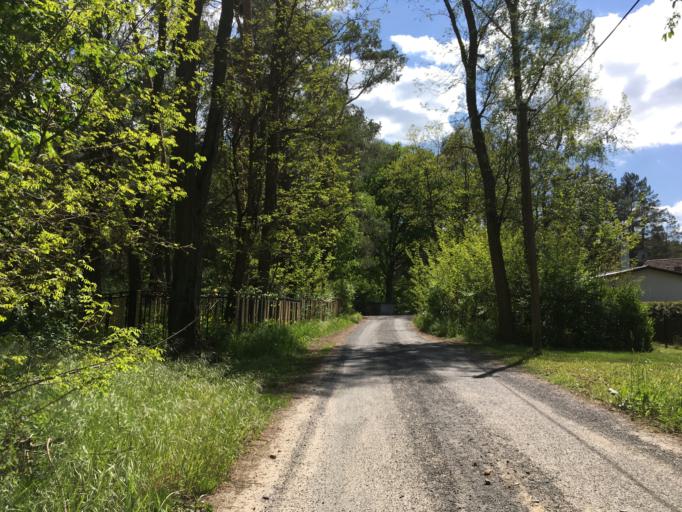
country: DE
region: Brandenburg
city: Rudnitz
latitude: 52.7217
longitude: 13.6584
